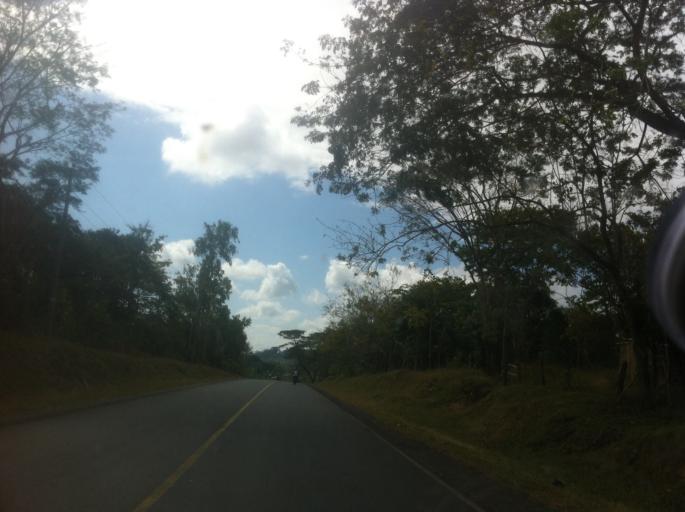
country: NI
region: Rio San Juan
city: San Carlos
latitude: 11.2667
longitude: -84.7150
